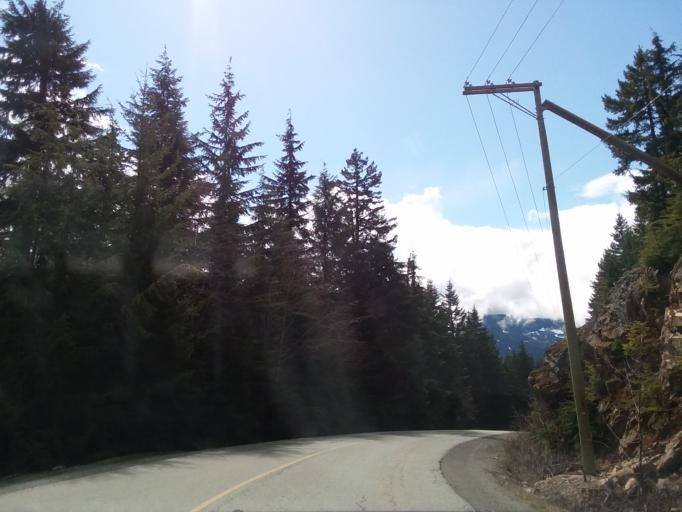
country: CA
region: British Columbia
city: Whistler
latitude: 50.1330
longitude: -122.9812
